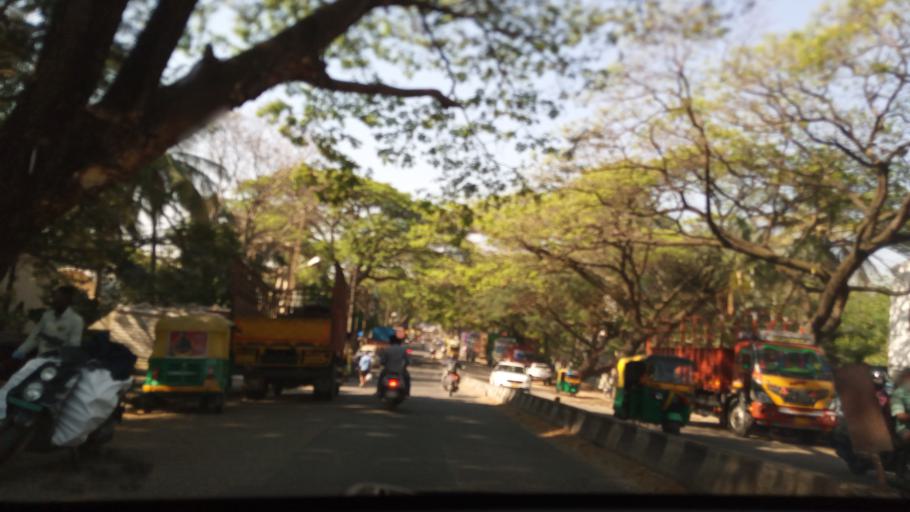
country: IN
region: Karnataka
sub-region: Bangalore Urban
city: Bangalore
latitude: 13.0226
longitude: 77.5420
